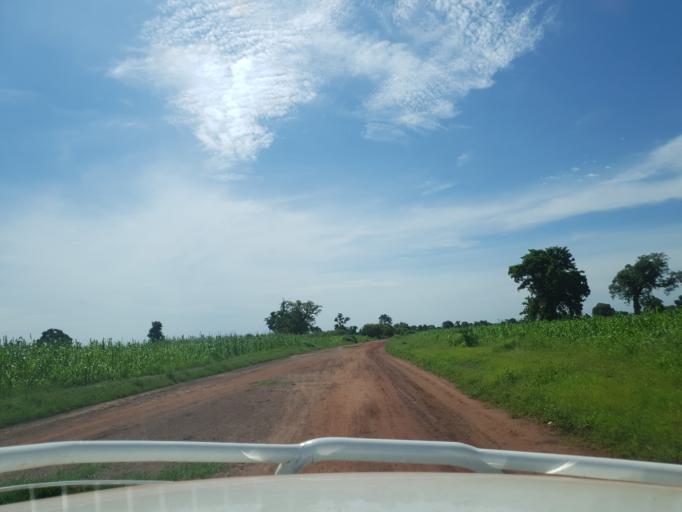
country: ML
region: Koulikoro
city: Banamba
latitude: 13.2794
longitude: -7.5506
